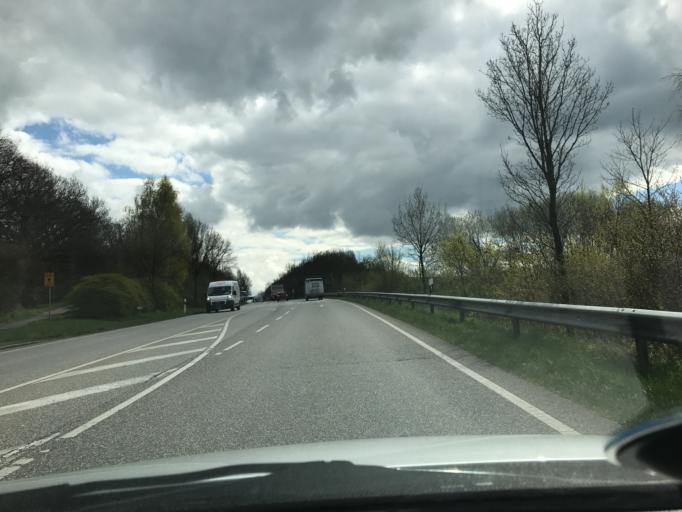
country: DE
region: Schleswig-Holstein
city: Susel
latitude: 54.0894
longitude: 10.6843
